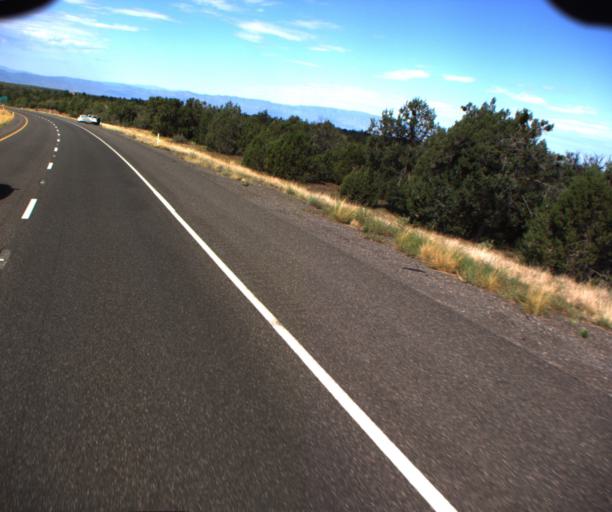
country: US
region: Arizona
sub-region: Yavapai County
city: Village of Oak Creek (Big Park)
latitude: 34.7762
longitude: -111.6348
